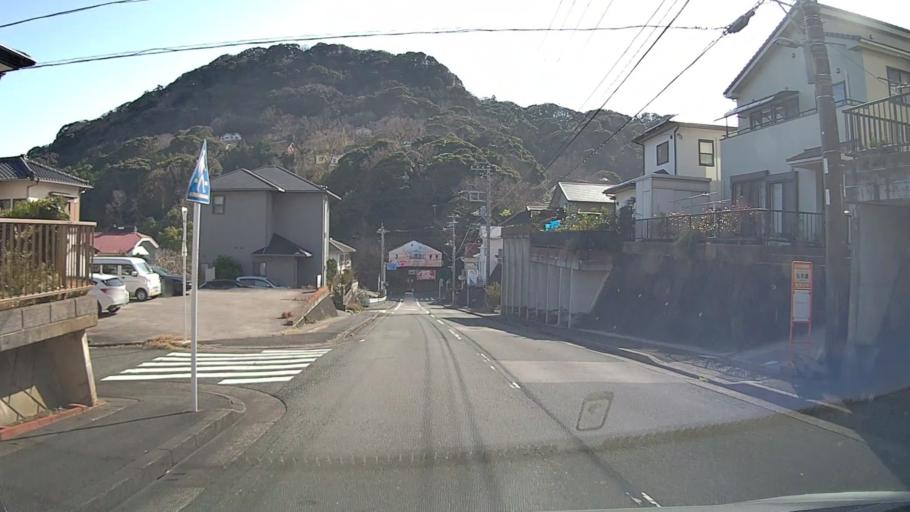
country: JP
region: Shizuoka
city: Shimoda
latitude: 34.6802
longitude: 138.9281
